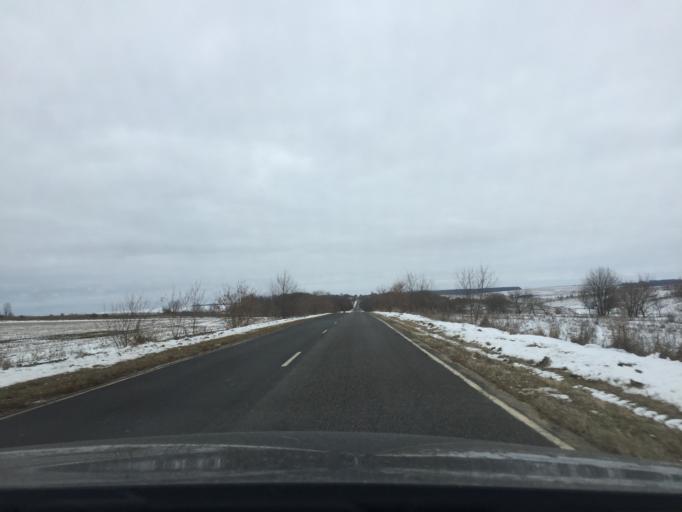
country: RU
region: Tula
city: Teploye
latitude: 53.7958
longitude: 37.5987
